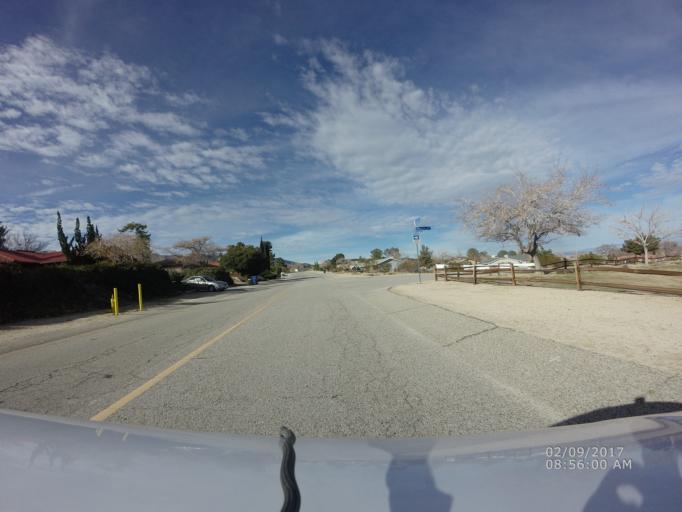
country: US
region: California
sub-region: Los Angeles County
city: Lake Los Angeles
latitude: 34.4736
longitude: -117.8395
